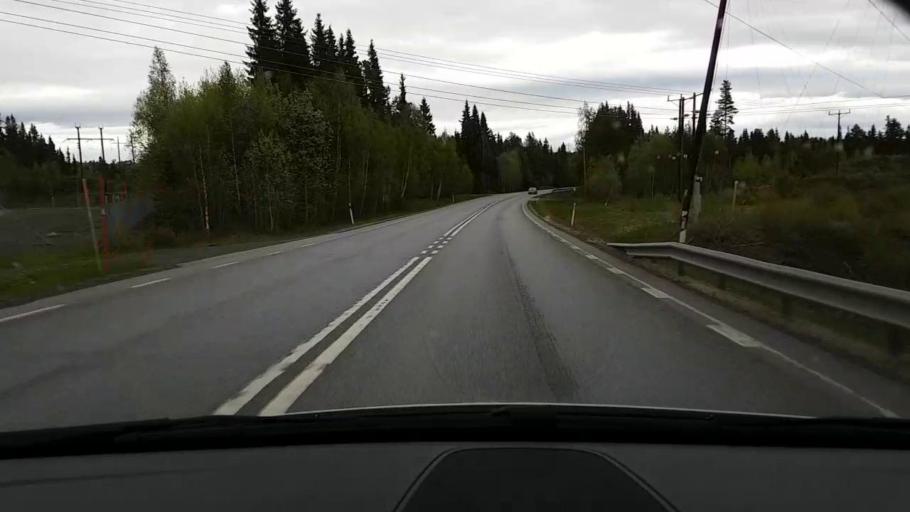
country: SE
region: Jaemtland
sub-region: Krokoms Kommun
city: Valla
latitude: 63.3348
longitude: 13.9780
